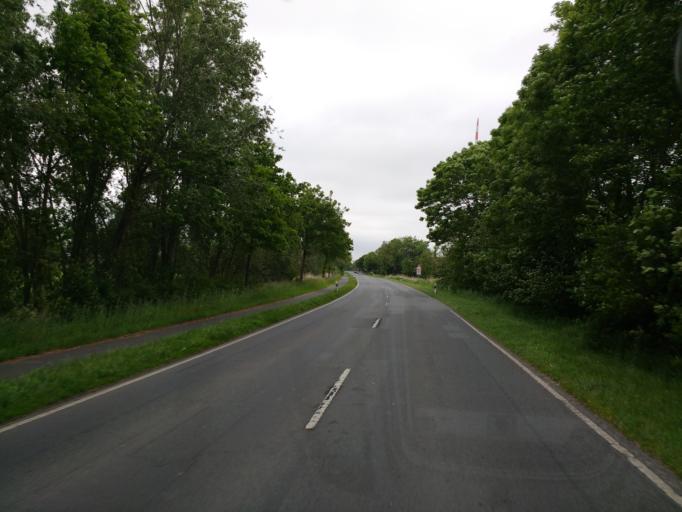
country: DE
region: Lower Saxony
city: Jever
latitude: 53.5896
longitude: 7.9157
